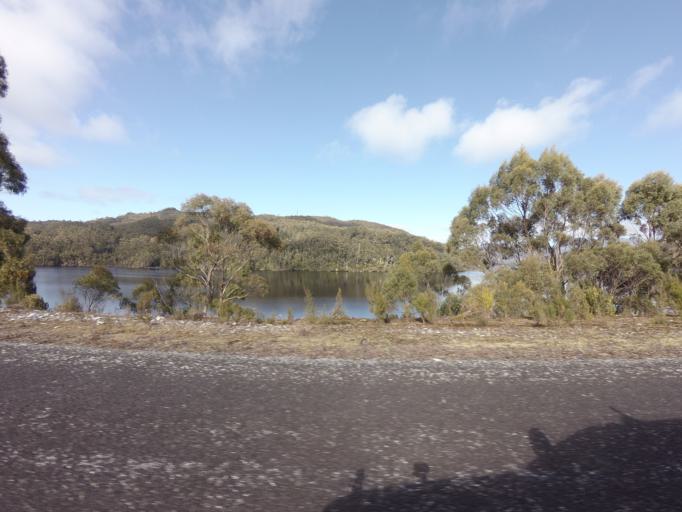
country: AU
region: Tasmania
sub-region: West Coast
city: Queenstown
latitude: -42.7974
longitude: 146.0879
